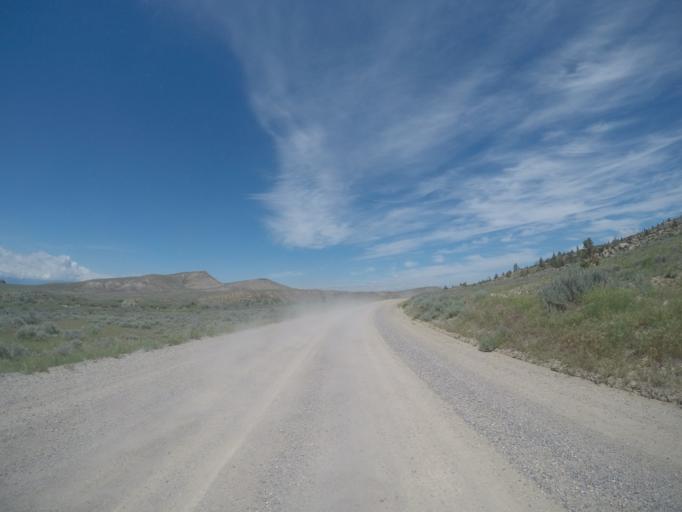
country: US
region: Montana
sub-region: Carbon County
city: Red Lodge
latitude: 45.2111
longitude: -108.8391
